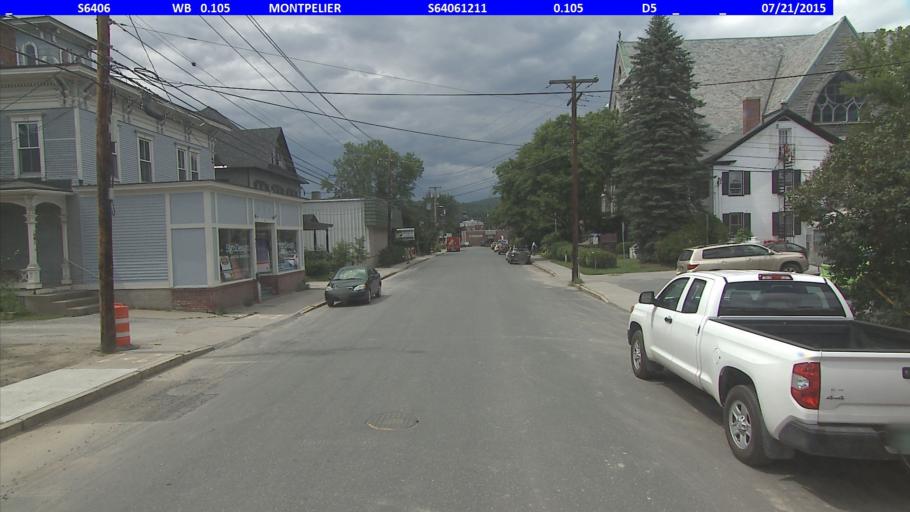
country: US
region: Vermont
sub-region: Washington County
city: Montpelier
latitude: 44.2576
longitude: -72.5753
